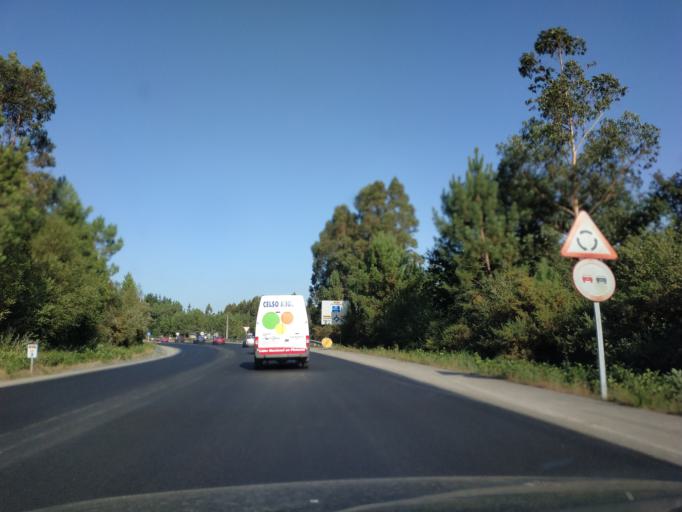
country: ES
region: Galicia
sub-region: Provincia da Coruna
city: Culleredo
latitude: 43.2594
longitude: -8.4182
